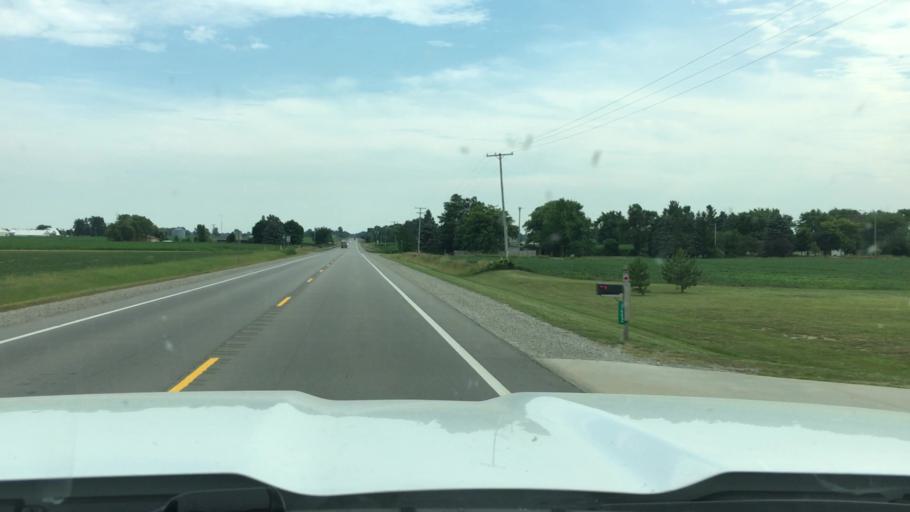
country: US
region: Michigan
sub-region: Sanilac County
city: Marlette
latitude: 43.3731
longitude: -83.0856
